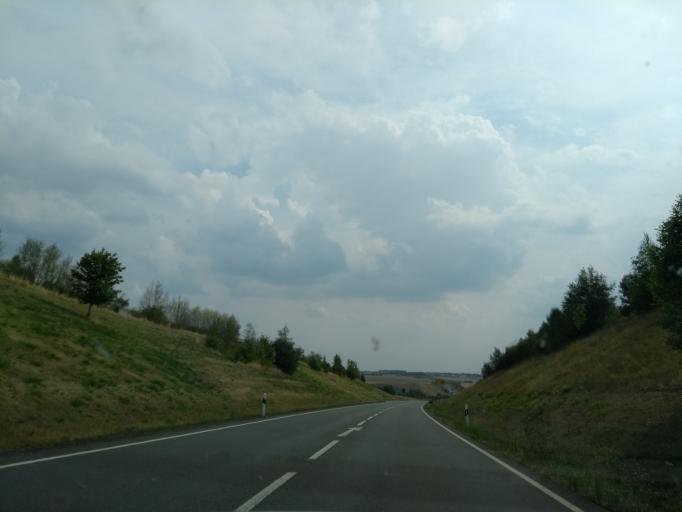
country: DE
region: Thuringia
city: Schwaara
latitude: 50.9240
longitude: 12.1348
